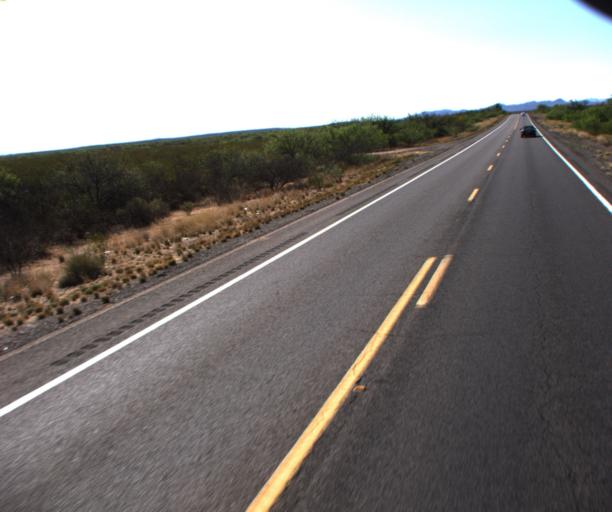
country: US
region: Arizona
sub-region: Cochise County
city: Saint David
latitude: 31.8032
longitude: -110.1596
